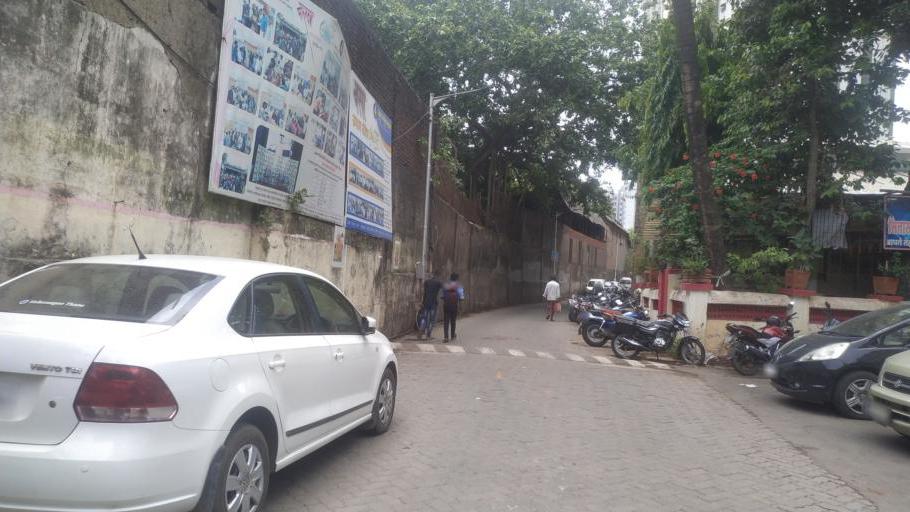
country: IN
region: Maharashtra
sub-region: Mumbai Suburban
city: Mumbai
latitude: 18.9888
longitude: 72.8374
